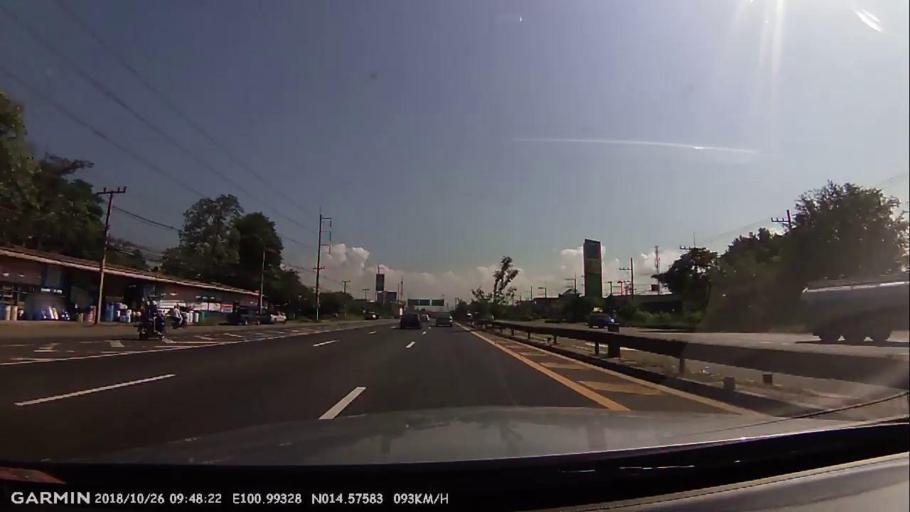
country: TH
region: Sara Buri
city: Kaeng Khoi
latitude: 14.5765
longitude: 100.9931
